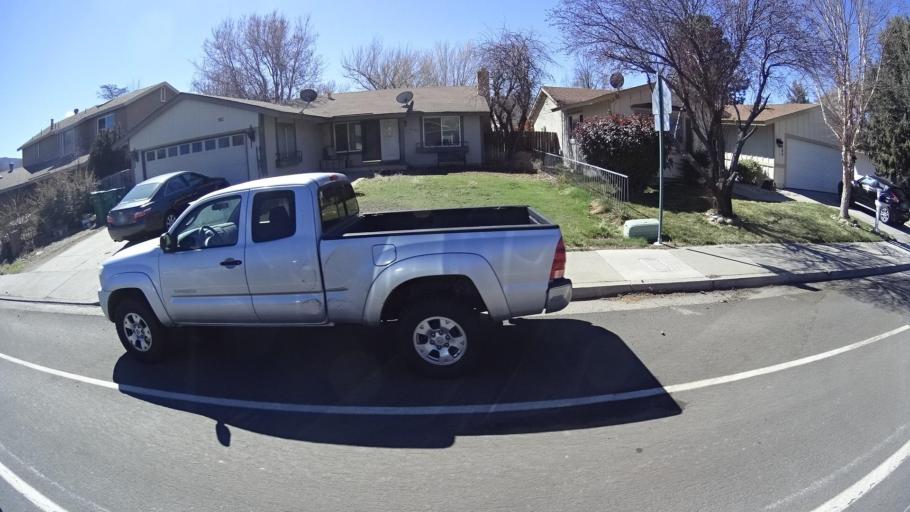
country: US
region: Nevada
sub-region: Washoe County
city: Sparks
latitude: 39.4860
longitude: -119.7505
